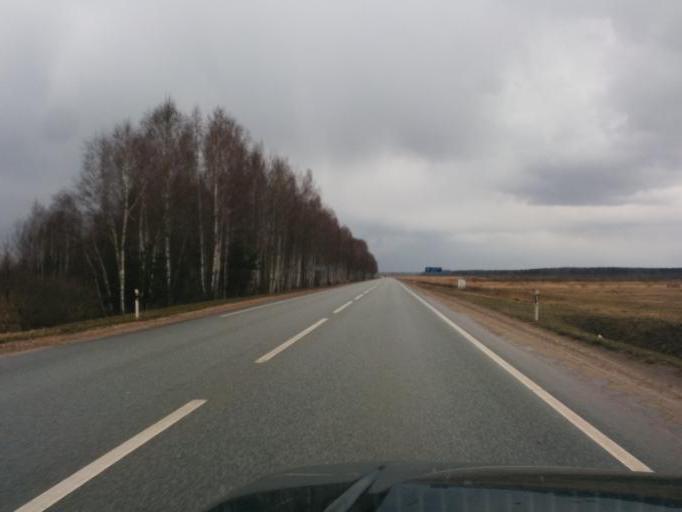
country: LV
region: Marupe
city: Marupe
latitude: 56.8491
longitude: 24.0099
